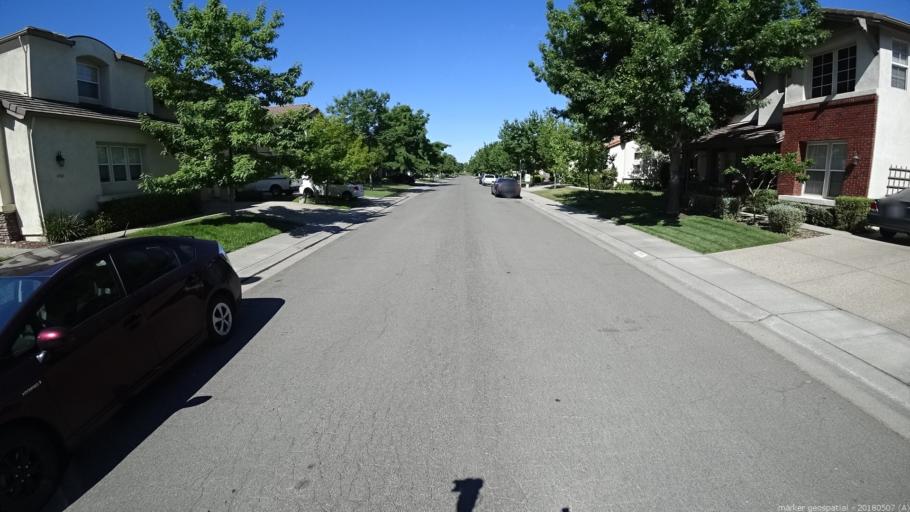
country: US
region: California
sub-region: Sacramento County
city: Rio Linda
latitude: 38.6610
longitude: -121.4977
